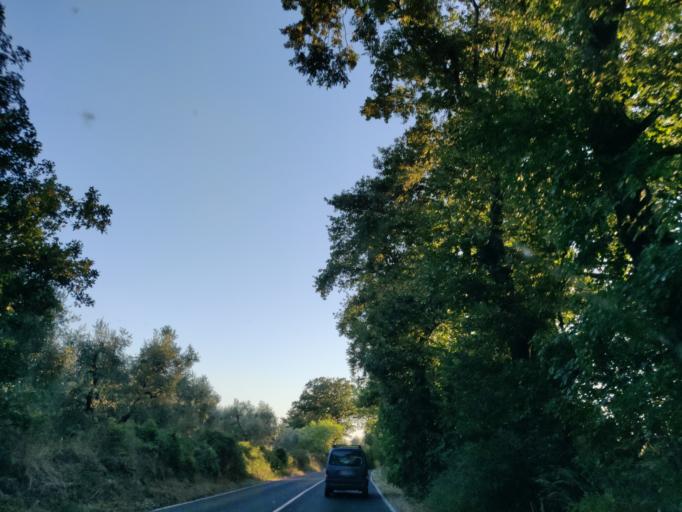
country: IT
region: Latium
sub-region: Provincia di Viterbo
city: Canino
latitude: 42.4404
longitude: 11.7300
